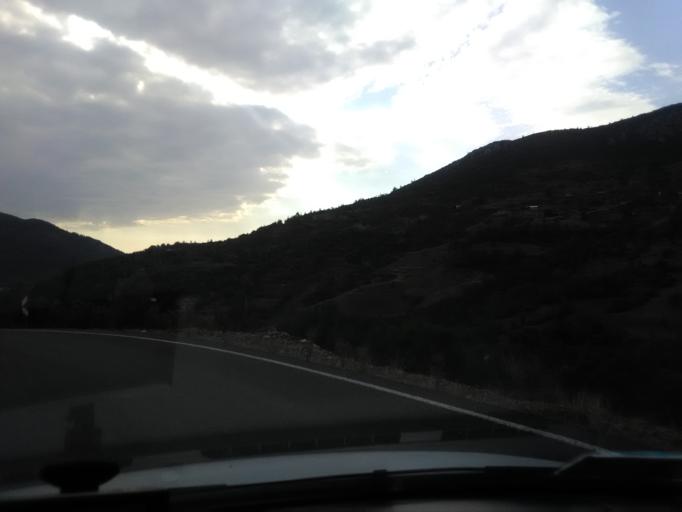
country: TR
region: Antalya
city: Gazipasa
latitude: 36.3023
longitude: 32.3808
